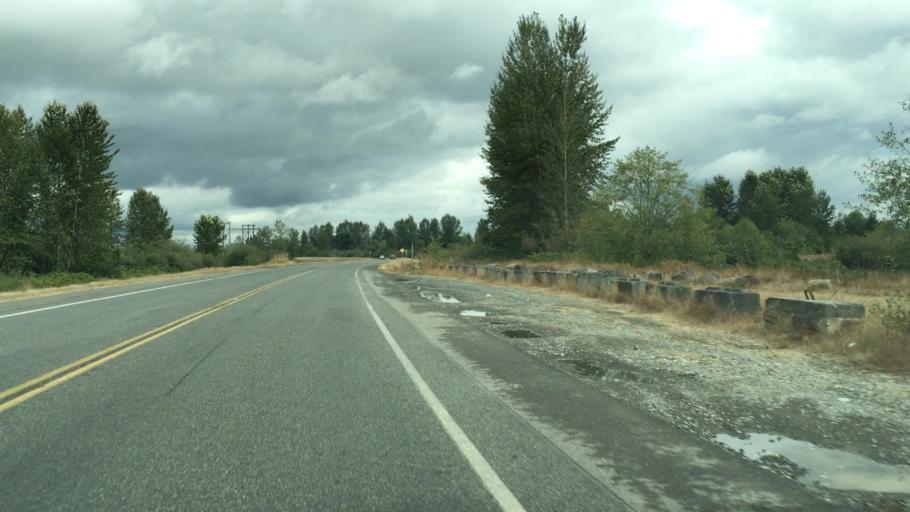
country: US
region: Washington
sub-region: Snohomish County
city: Everett
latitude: 47.9338
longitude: -122.1722
